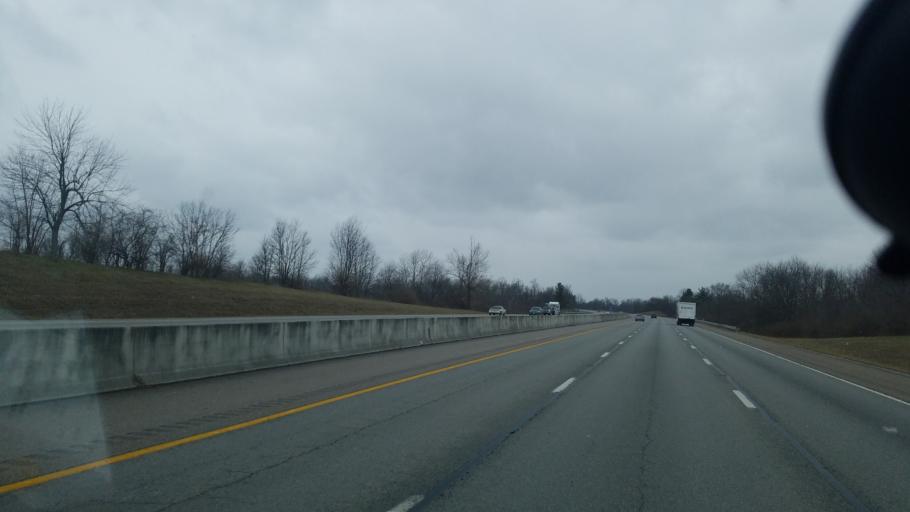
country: US
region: Kentucky
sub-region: Fayette County
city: Lexington-Fayette
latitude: 38.0592
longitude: -84.3738
